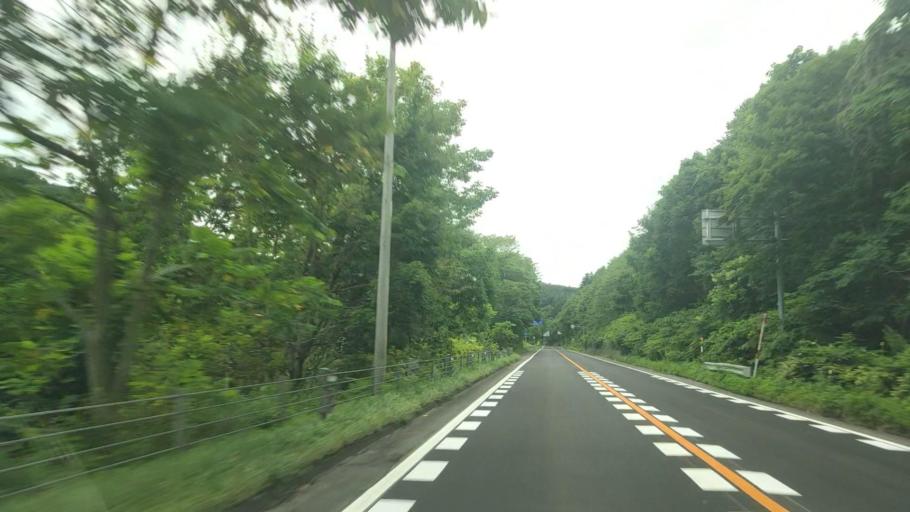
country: JP
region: Hokkaido
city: Niseko Town
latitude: 42.5989
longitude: 140.6061
